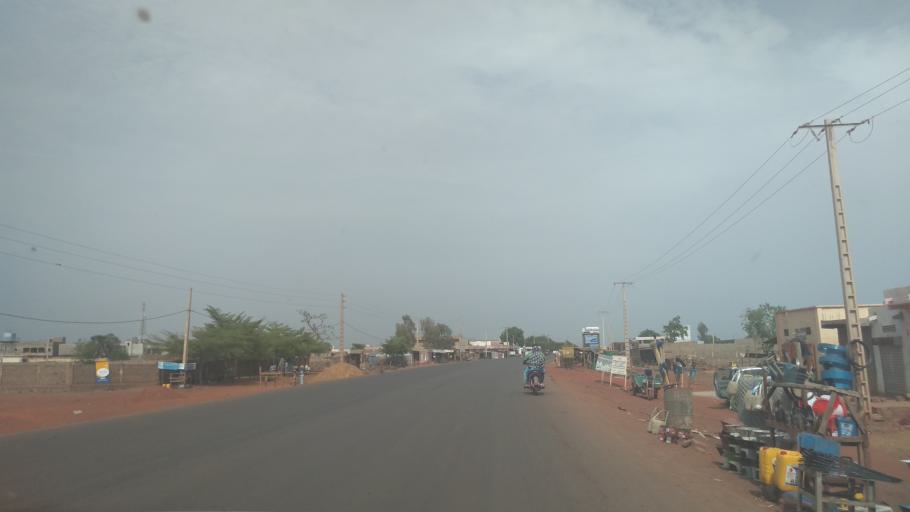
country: ML
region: Bamako
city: Bamako
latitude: 12.5871
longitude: -7.8321
